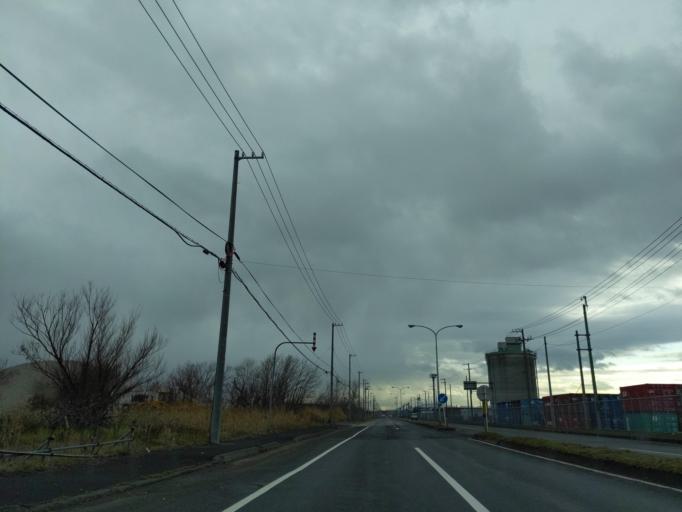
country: JP
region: Hokkaido
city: Ishikari
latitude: 43.1934
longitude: 141.2945
